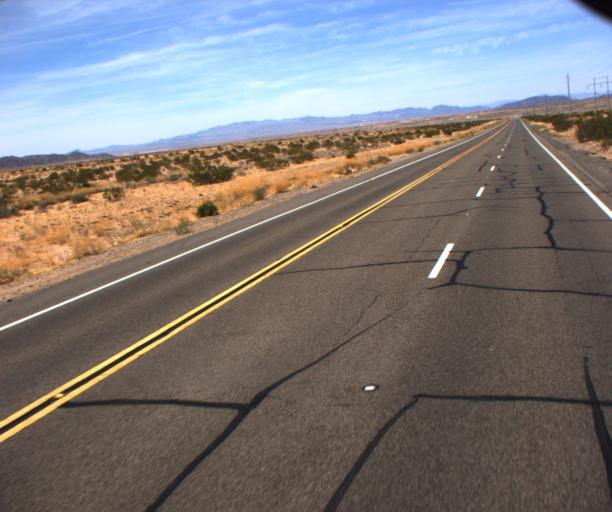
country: US
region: Arizona
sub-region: La Paz County
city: Parker
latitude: 33.9607
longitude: -114.2169
